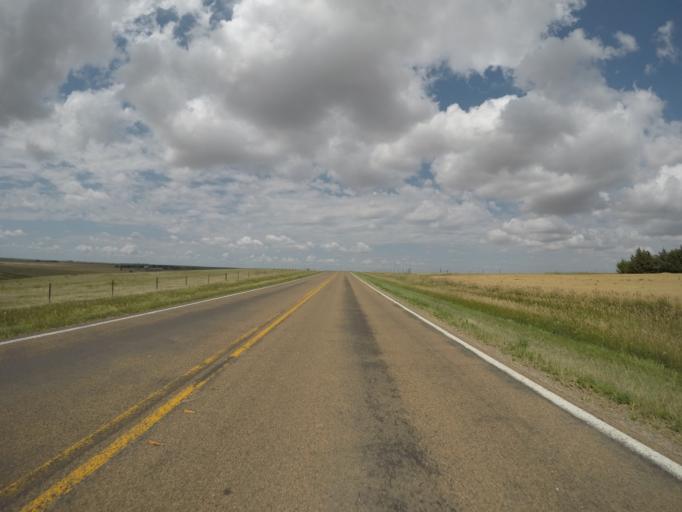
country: US
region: Kansas
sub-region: Rawlins County
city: Atwood
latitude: 39.9180
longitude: -101.0562
